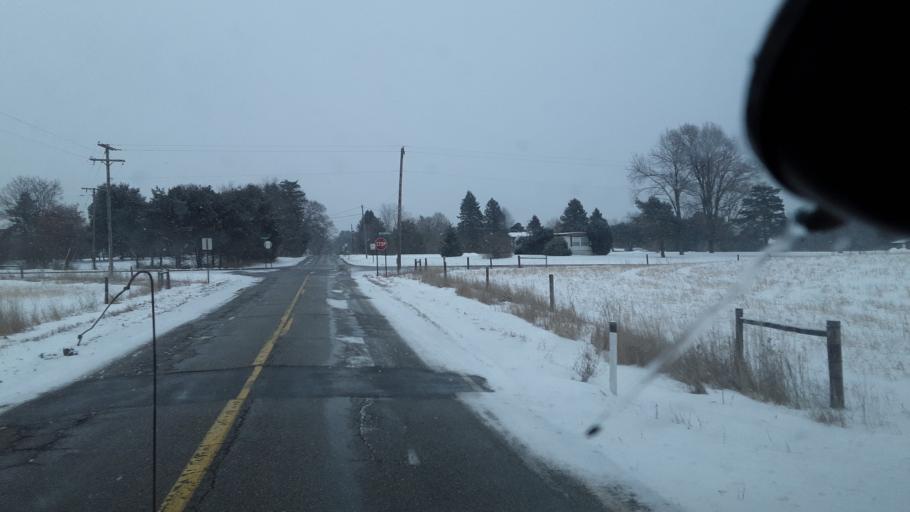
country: US
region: Michigan
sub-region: Ingham County
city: Leslie
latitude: 42.4898
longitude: -84.3179
